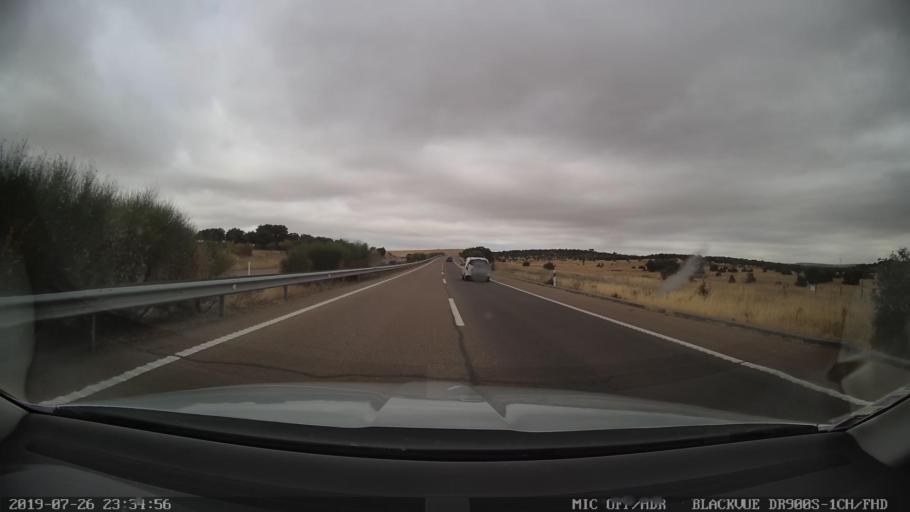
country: ES
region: Extremadura
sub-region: Provincia de Caceres
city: Santa Cruz de la Sierra
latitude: 39.3678
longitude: -5.8742
